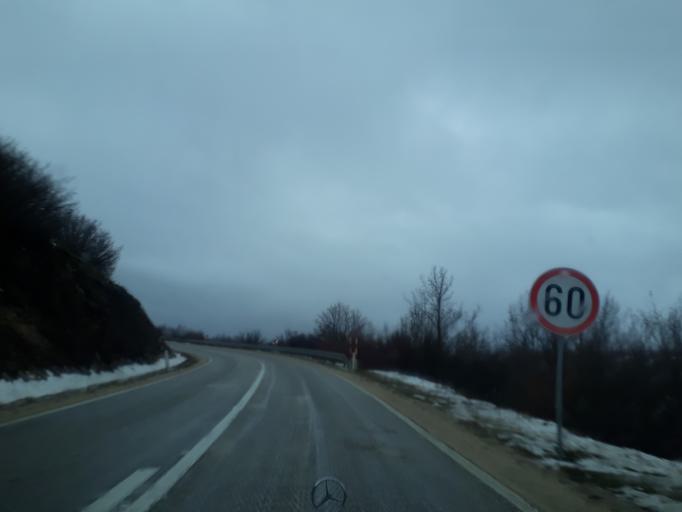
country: BA
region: Federation of Bosnia and Herzegovina
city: Tomislavgrad
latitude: 43.8024
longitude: 17.2049
